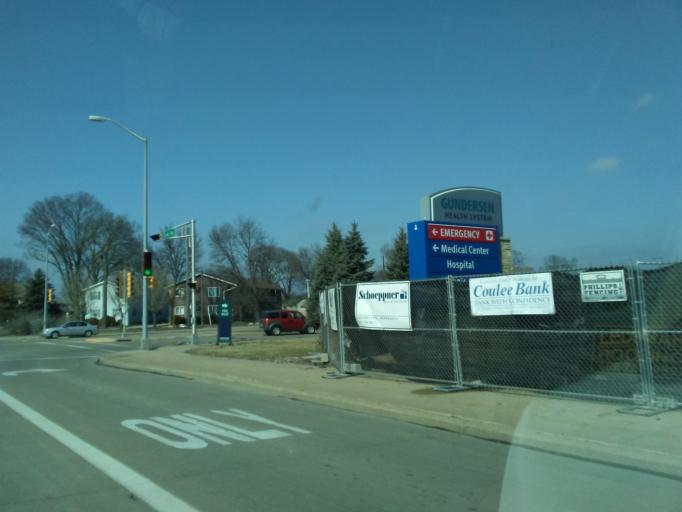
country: US
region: Wisconsin
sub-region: La Crosse County
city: La Crosse
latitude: 43.7963
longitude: -91.2485
